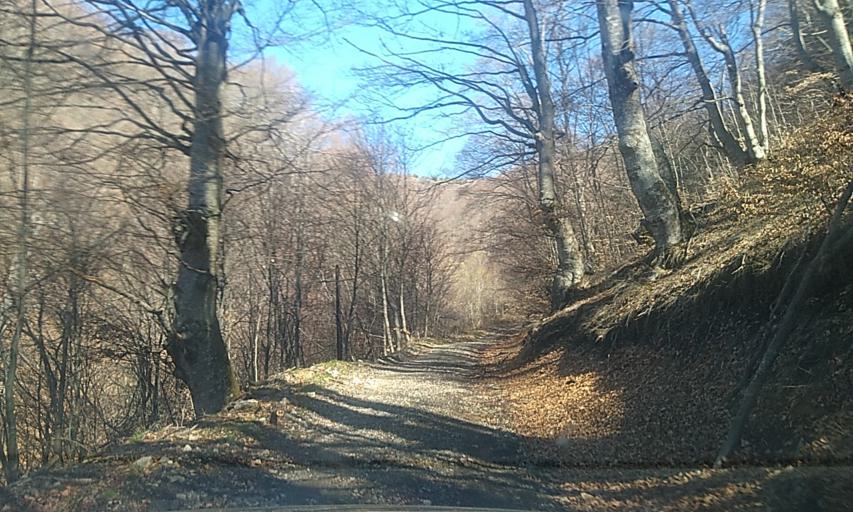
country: RS
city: Radovnica
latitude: 42.3522
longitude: 22.3375
